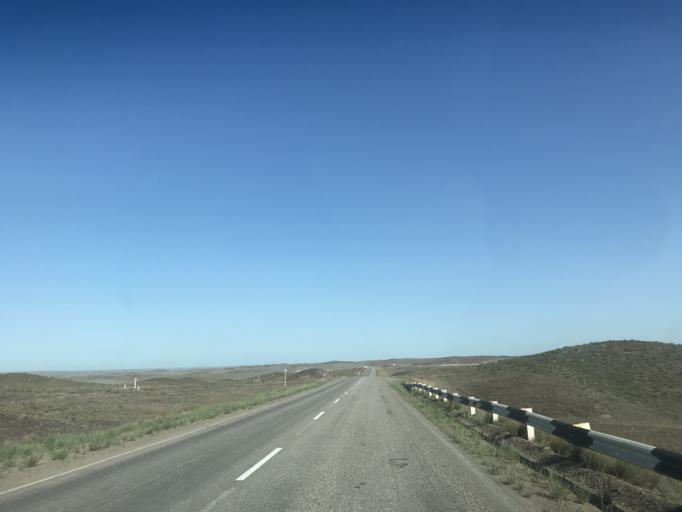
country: KZ
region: Zhambyl
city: Mynaral
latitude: 45.4615
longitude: 73.5783
